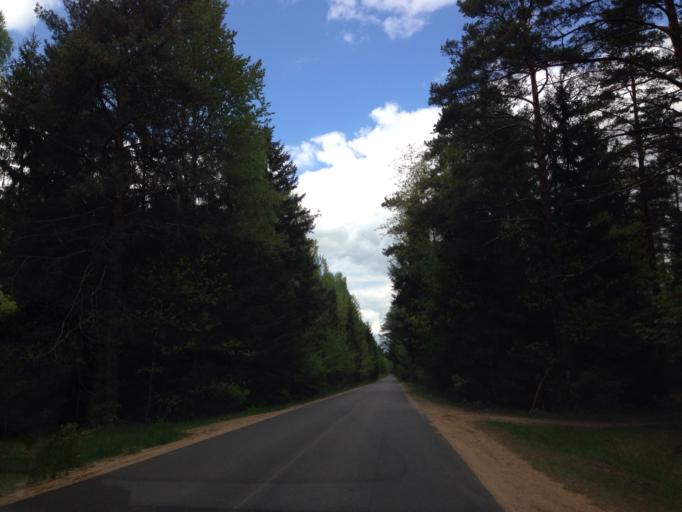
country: PL
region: Podlasie
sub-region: Powiat grajewski
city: Radzilow
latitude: 53.3343
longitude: 22.5993
